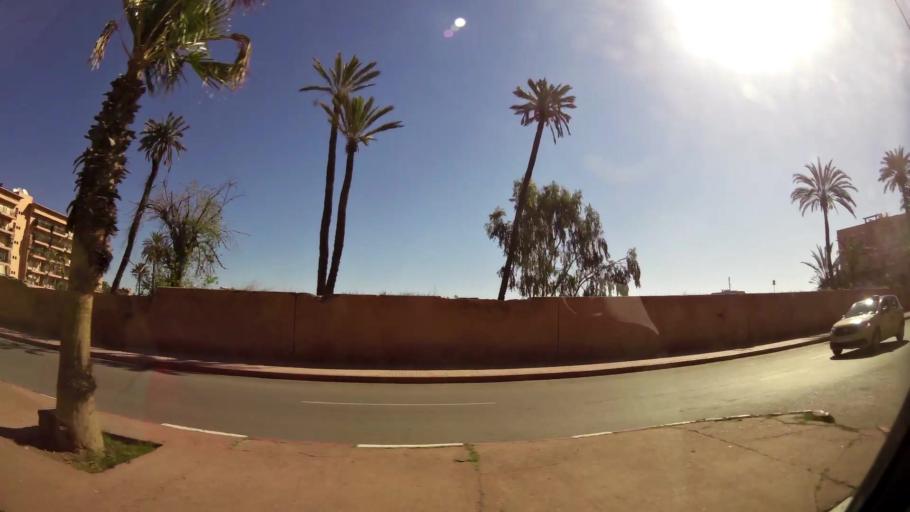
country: MA
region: Marrakech-Tensift-Al Haouz
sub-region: Marrakech
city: Marrakesh
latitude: 31.6380
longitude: -8.0033
